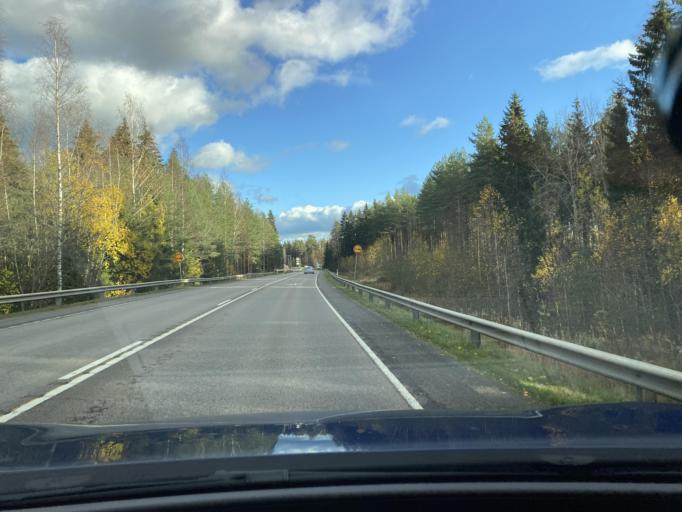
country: FI
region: Haeme
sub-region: Riihimaeki
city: Oitti
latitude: 60.7926
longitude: 24.9896
